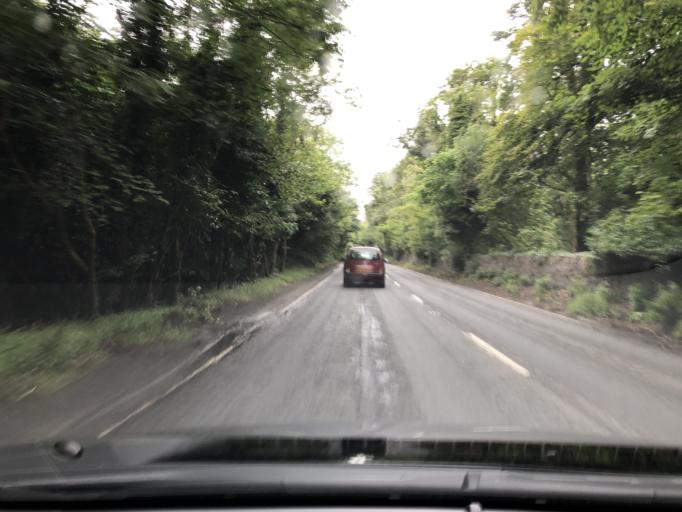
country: GB
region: Northern Ireland
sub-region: Down District
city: Dundrum
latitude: 54.3139
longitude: -5.8401
